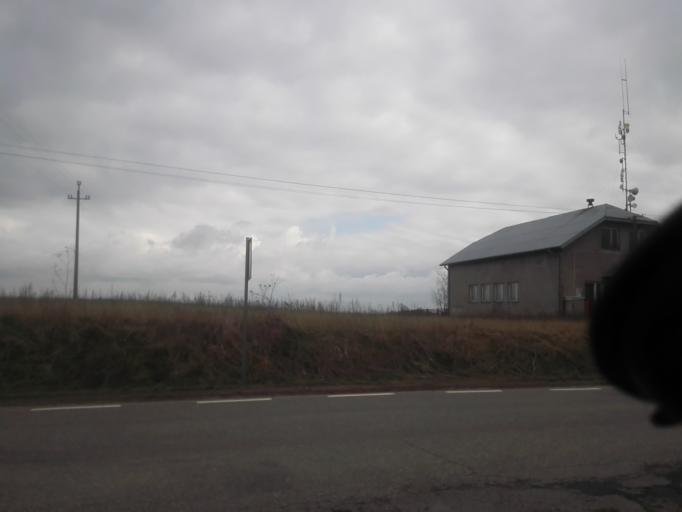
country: PL
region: Podlasie
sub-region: Suwalki
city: Suwalki
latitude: 54.2503
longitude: 22.9171
